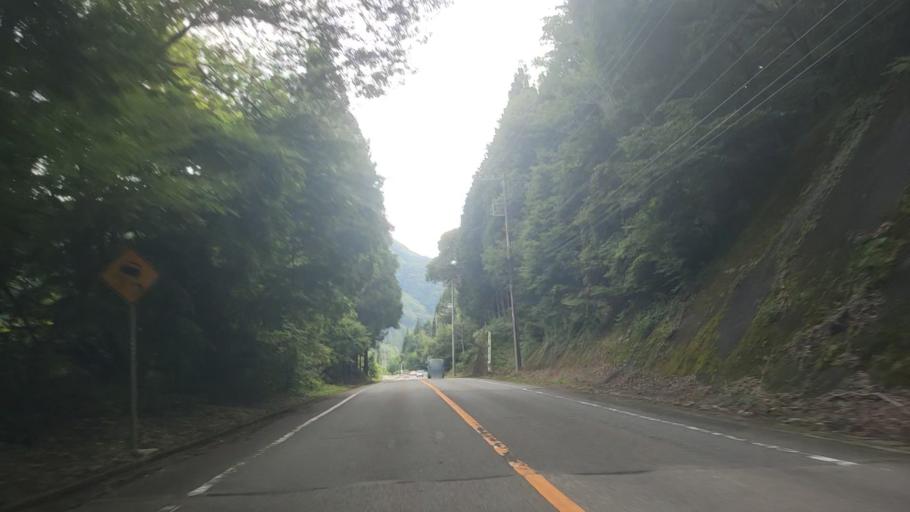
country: JP
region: Gunma
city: Kiryu
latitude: 36.5870
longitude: 139.3989
